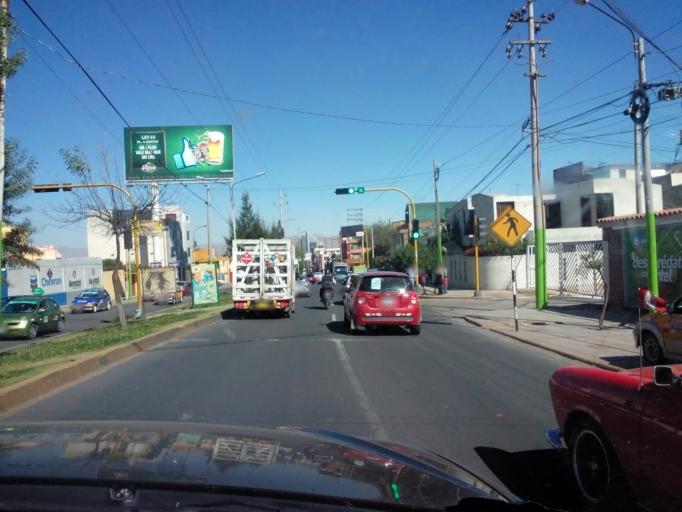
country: PE
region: Arequipa
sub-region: Provincia de Arequipa
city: Arequipa
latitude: -16.3766
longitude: -71.5571
